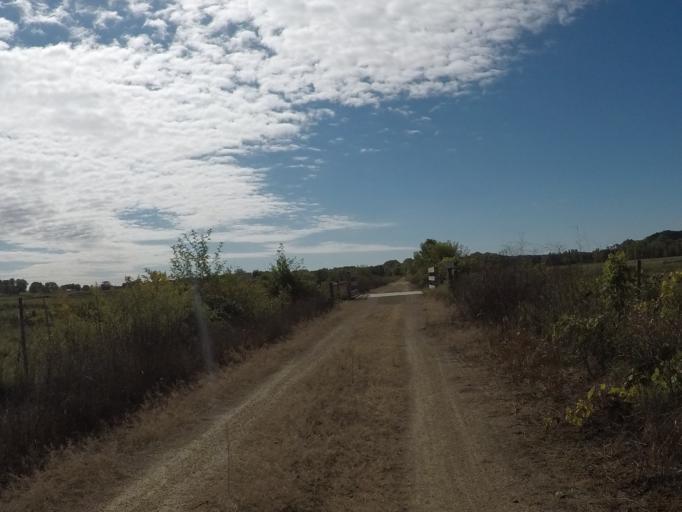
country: US
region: Wisconsin
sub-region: Richland County
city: Richland Center
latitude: 43.2353
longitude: -90.3002
